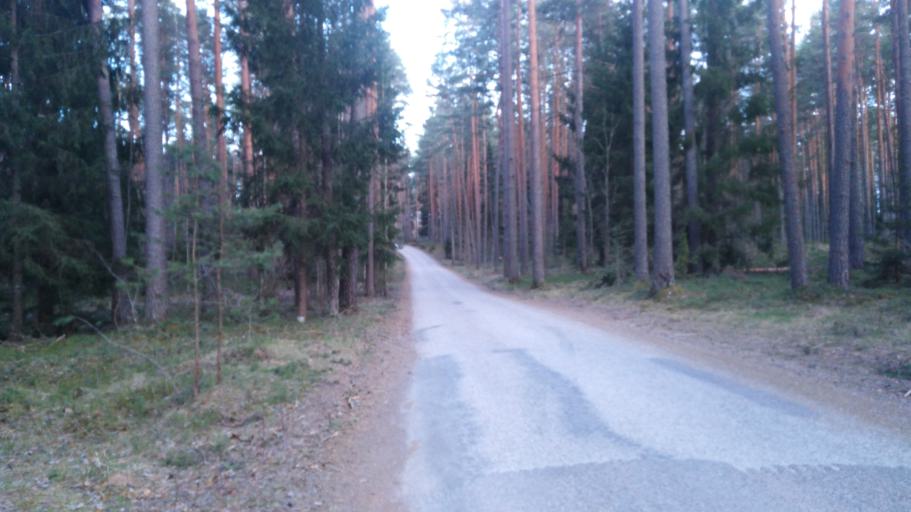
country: EE
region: Vorumaa
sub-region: Voru linn
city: Voru
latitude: 57.8104
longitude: 27.0077
